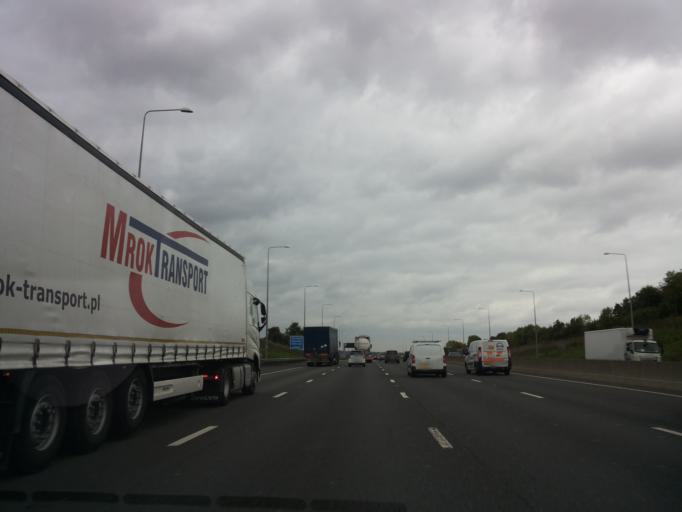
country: GB
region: England
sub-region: Hertfordshire
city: Shenley AV
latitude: 51.7078
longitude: -0.2567
